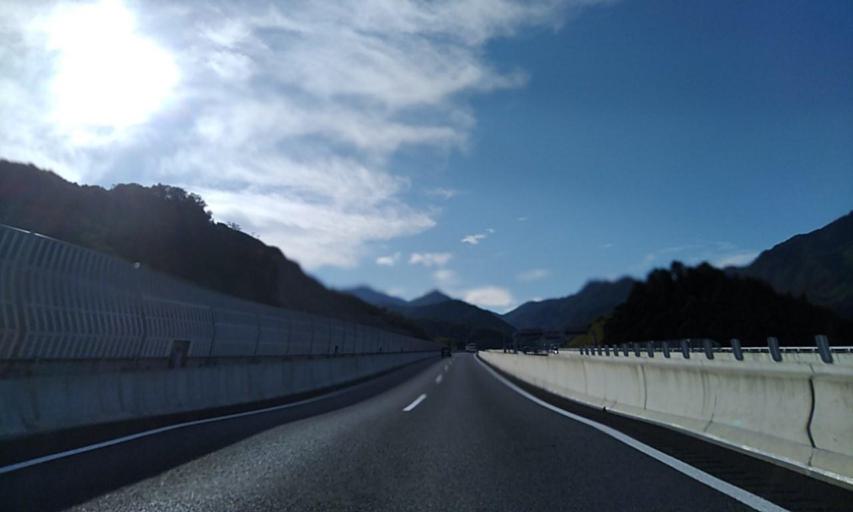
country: JP
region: Mie
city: Kameyama
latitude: 34.9160
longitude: 136.4002
